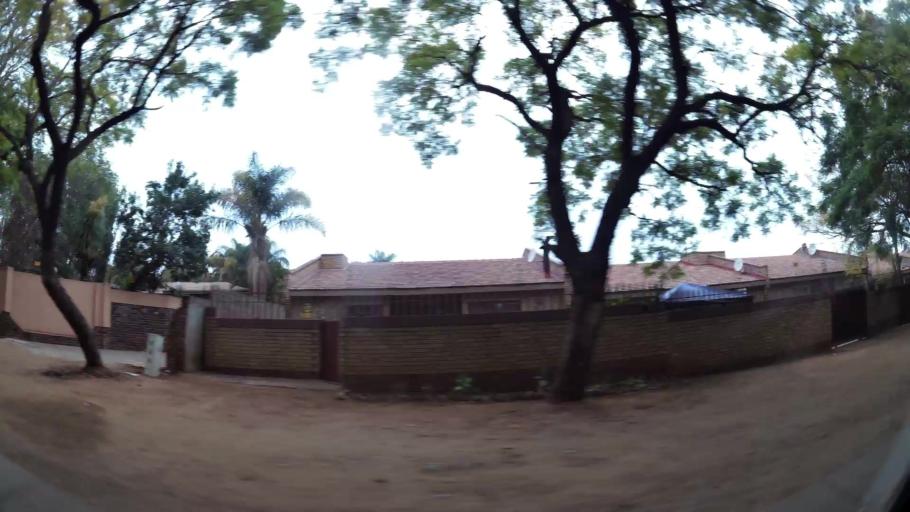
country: ZA
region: Limpopo
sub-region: Capricorn District Municipality
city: Polokwane
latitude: -23.9026
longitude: 29.4626
